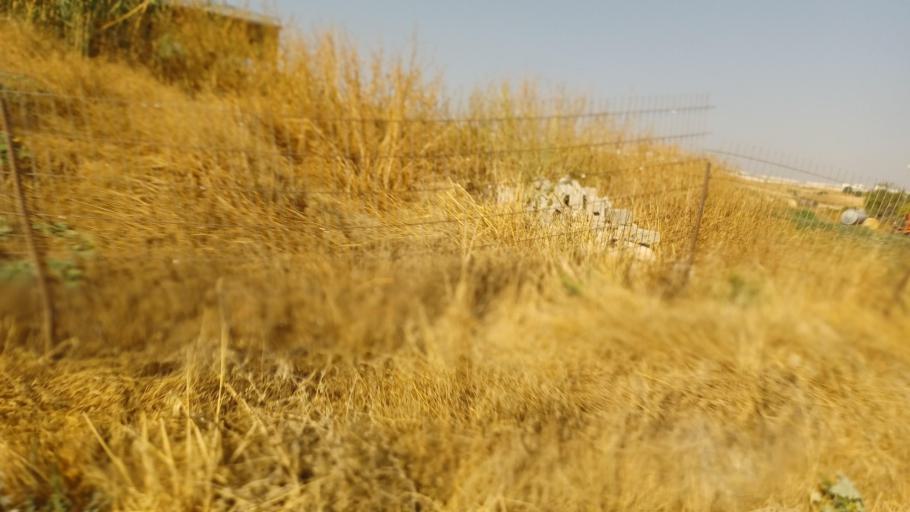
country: CY
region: Lefkosia
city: Lympia
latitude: 34.9893
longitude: 33.4707
